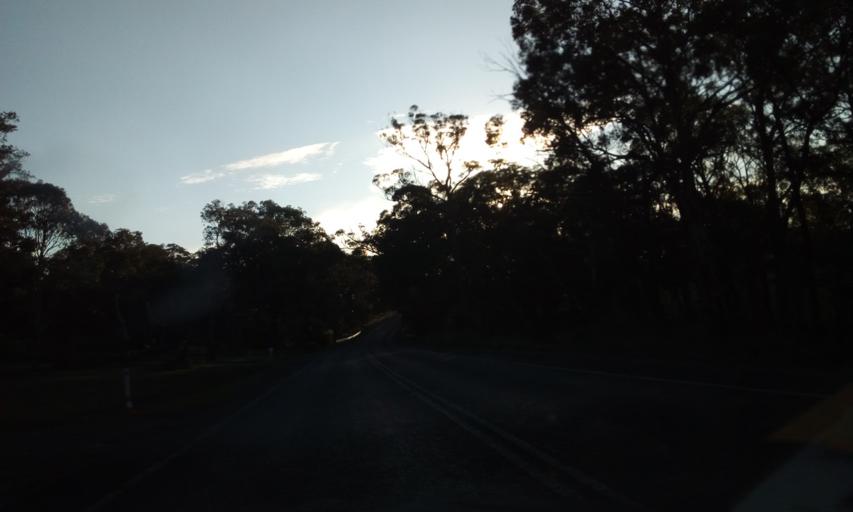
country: AU
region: New South Wales
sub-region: Wollondilly
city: Douglas Park
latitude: -34.2401
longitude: 150.7183
